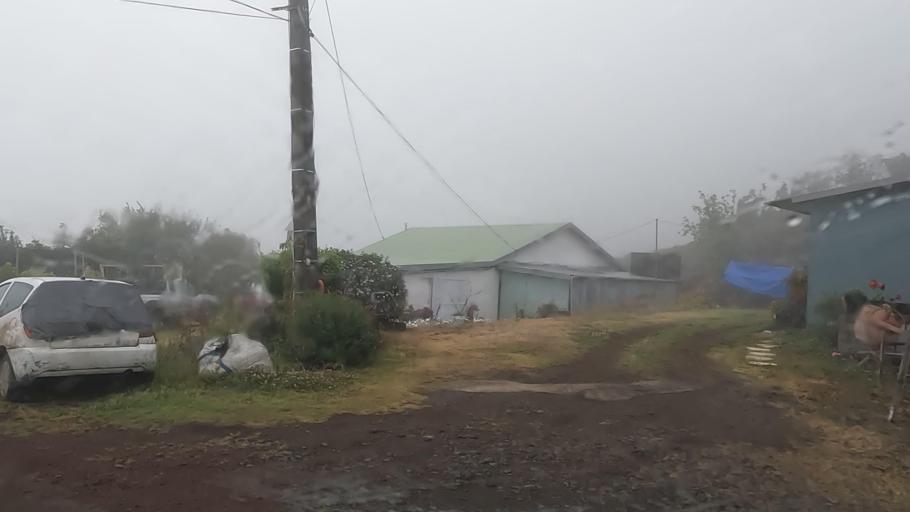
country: RE
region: Reunion
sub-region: Reunion
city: Le Tampon
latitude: -21.2074
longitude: 55.5880
